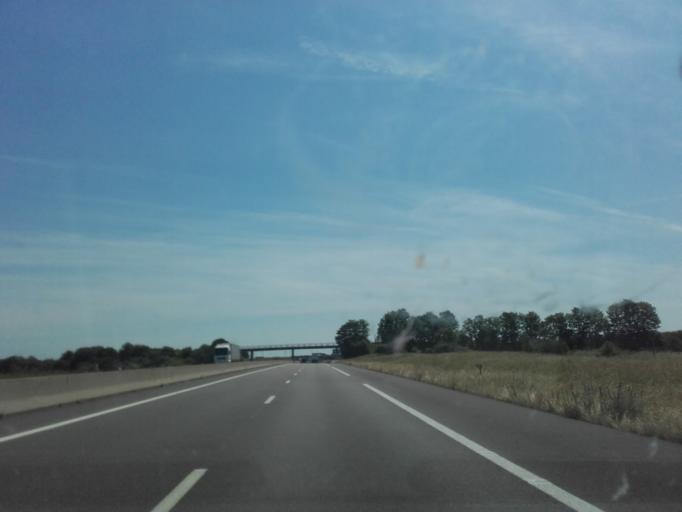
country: FR
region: Bourgogne
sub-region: Departement de la Cote-d'Or
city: Semur-en-Auxois
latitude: 47.4883
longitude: 4.1452
